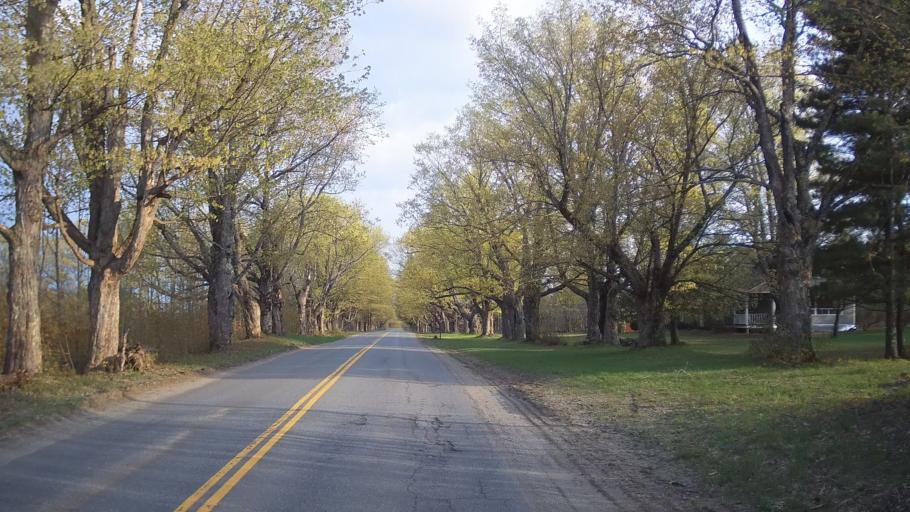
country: US
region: Vermont
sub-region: Orleans County
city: Newport
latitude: 44.9093
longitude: -72.4316
